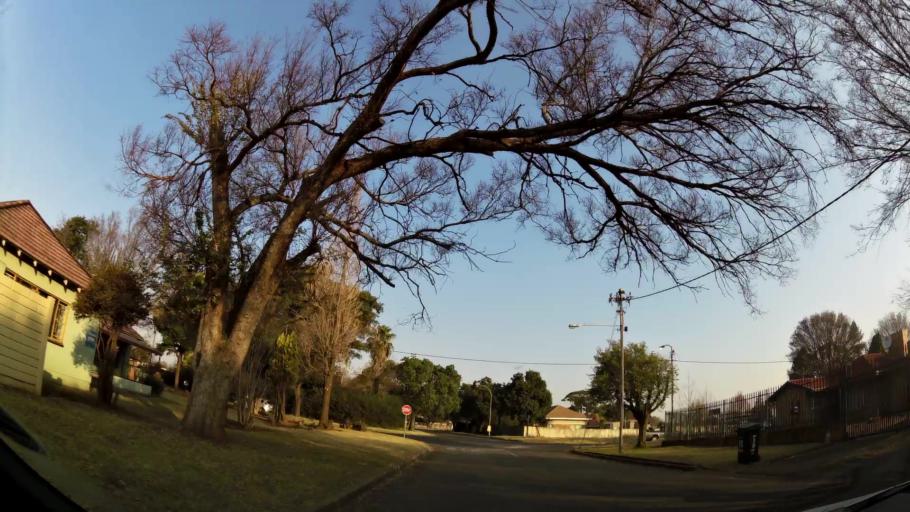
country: ZA
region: Gauteng
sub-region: Ekurhuleni Metropolitan Municipality
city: Springs
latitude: -26.2944
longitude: 28.4419
